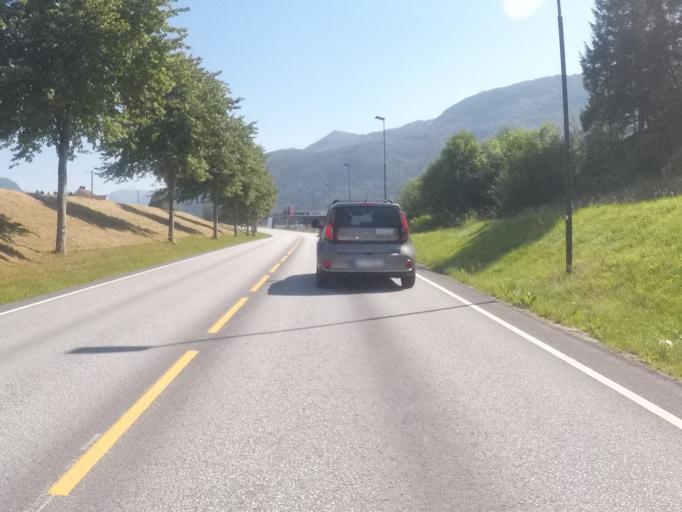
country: NO
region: Sogn og Fjordane
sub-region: Eid
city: Nordfjordeid
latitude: 61.9109
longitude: 5.9933
